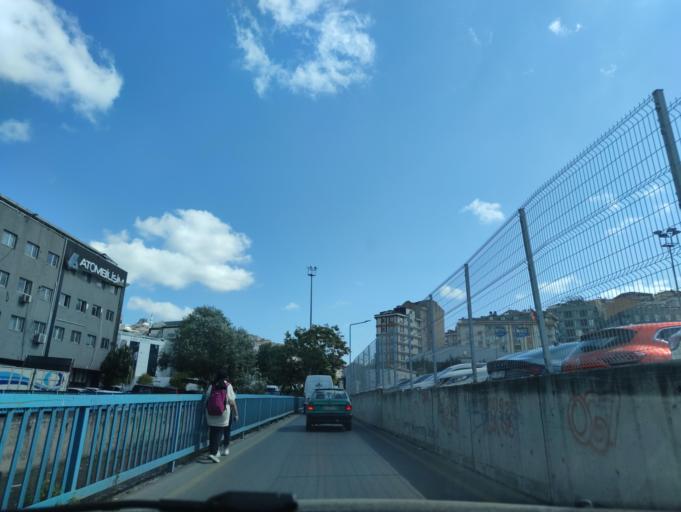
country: TR
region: Istanbul
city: Sisli
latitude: 41.0840
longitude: 28.9834
